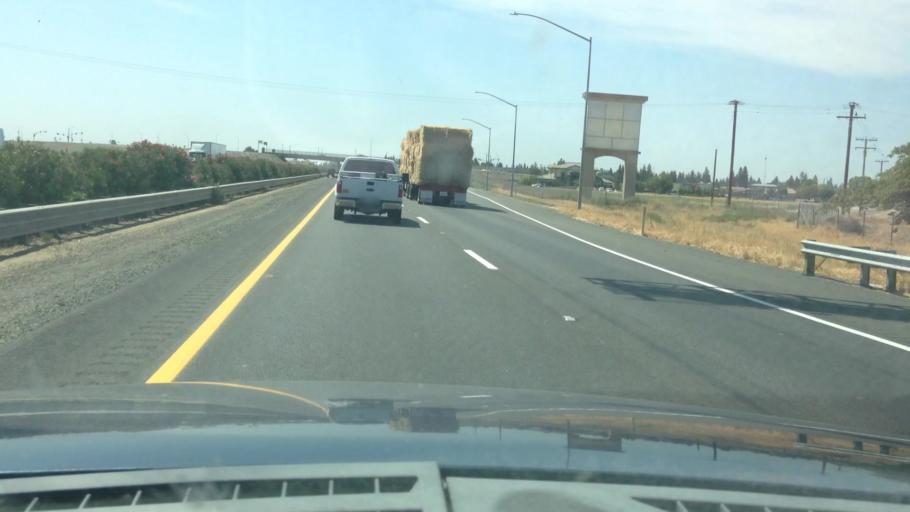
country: US
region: California
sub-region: Tulare County
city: Tulare
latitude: 36.2432
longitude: -119.3452
